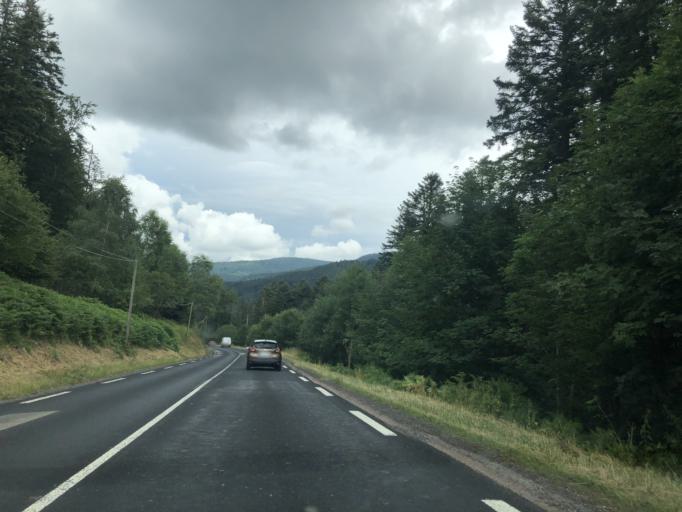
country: FR
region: Lorraine
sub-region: Departement des Vosges
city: Xonrupt-Longemer
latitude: 48.0891
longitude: 6.9026
